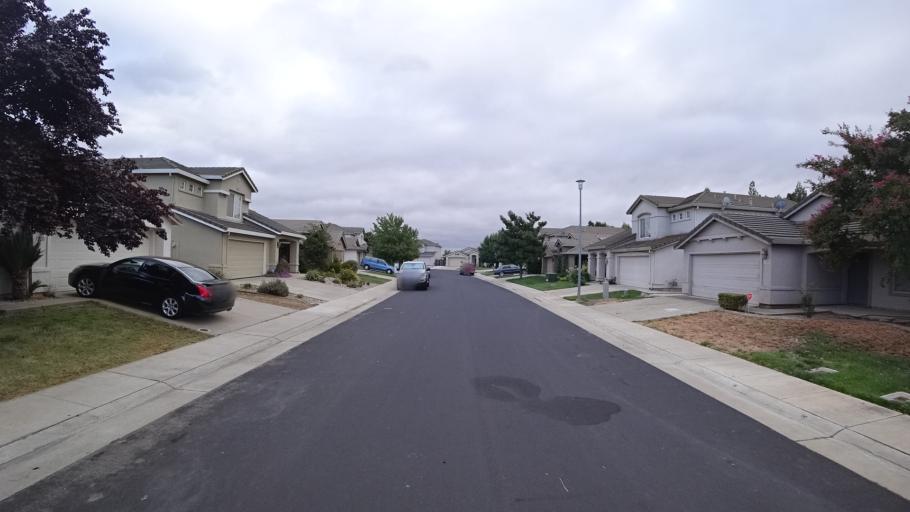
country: US
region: California
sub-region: Sacramento County
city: Laguna
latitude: 38.4311
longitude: -121.4204
